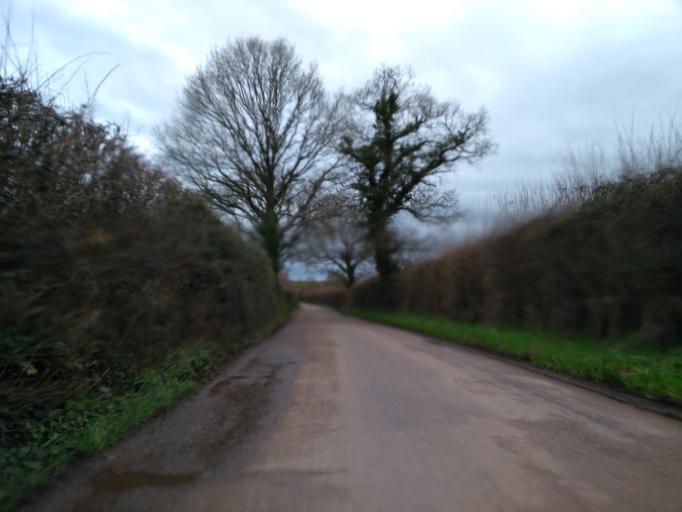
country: GB
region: England
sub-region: Devon
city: Bradninch
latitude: 50.8054
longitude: -3.4878
